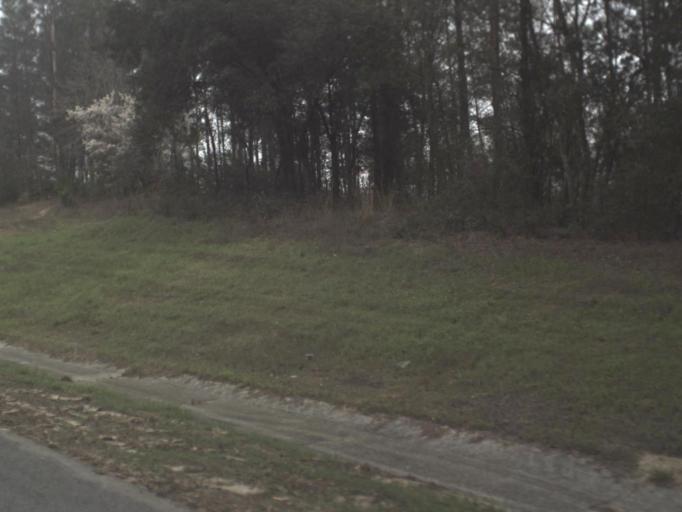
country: US
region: Florida
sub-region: Gadsden County
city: Gretna
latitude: 30.4640
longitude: -84.7382
